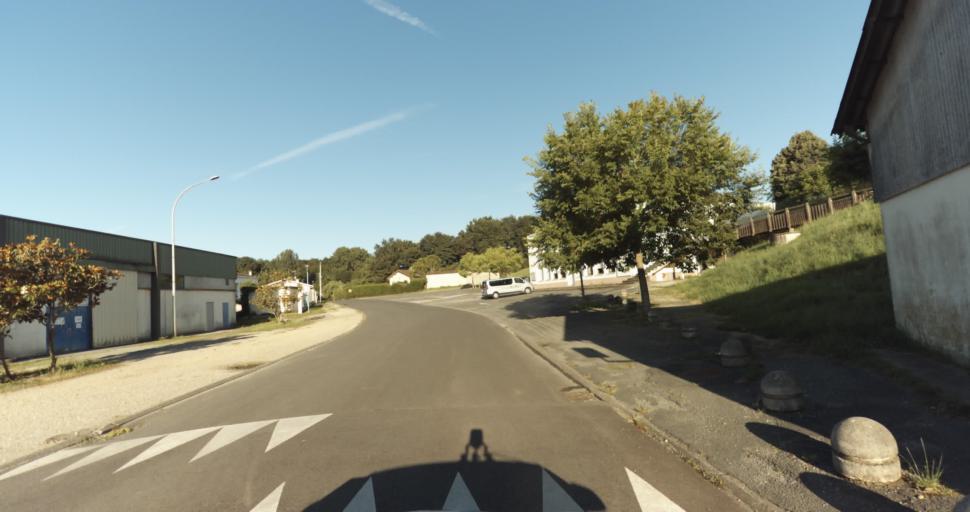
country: FR
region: Aquitaine
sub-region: Departement de la Gironde
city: Bazas
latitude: 44.4311
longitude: -0.2177
